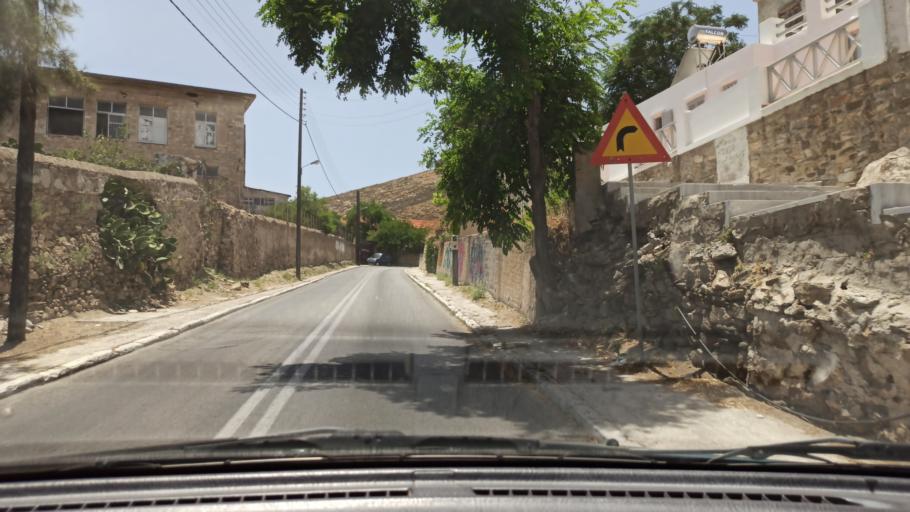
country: GR
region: South Aegean
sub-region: Nomos Kykladon
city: Ermoupolis
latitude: 37.4310
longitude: 24.9347
